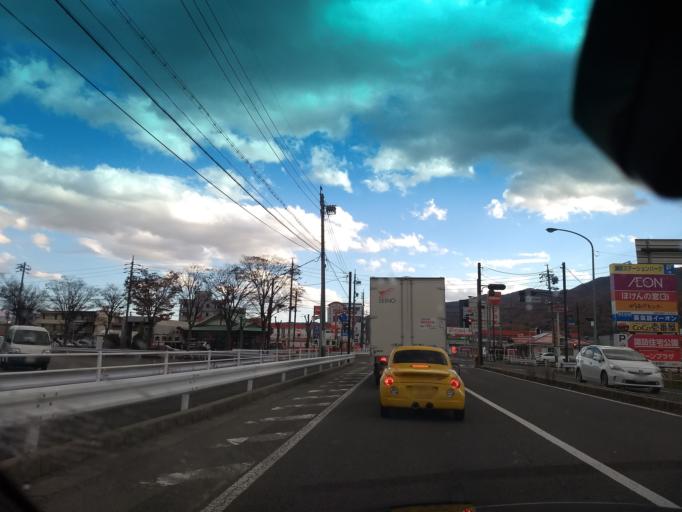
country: JP
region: Nagano
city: Chino
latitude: 36.0059
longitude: 138.1313
